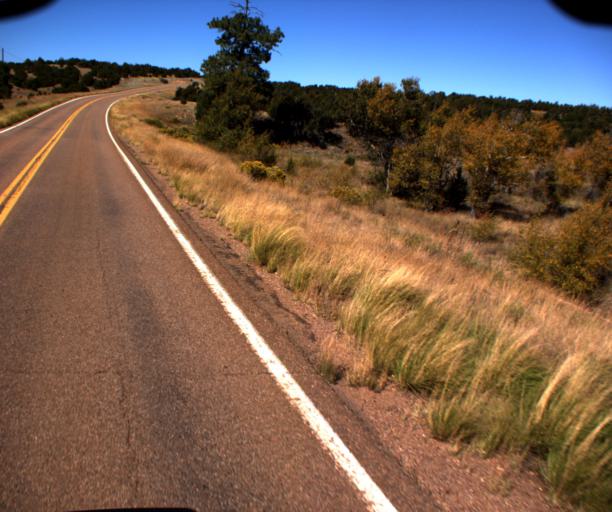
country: US
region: Arizona
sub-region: Navajo County
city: Heber-Overgaard
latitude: 34.4530
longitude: -110.4585
